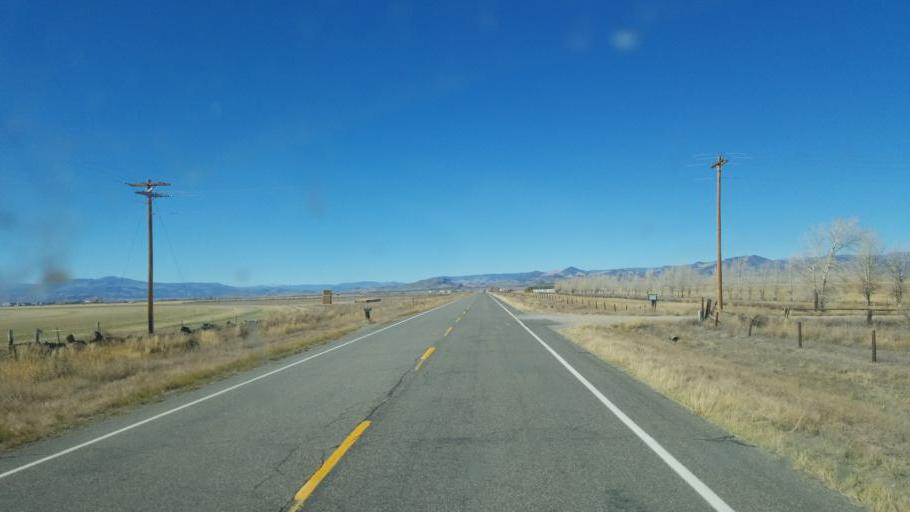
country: US
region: Colorado
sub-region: Saguache County
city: Center
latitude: 37.7481
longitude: -106.1807
